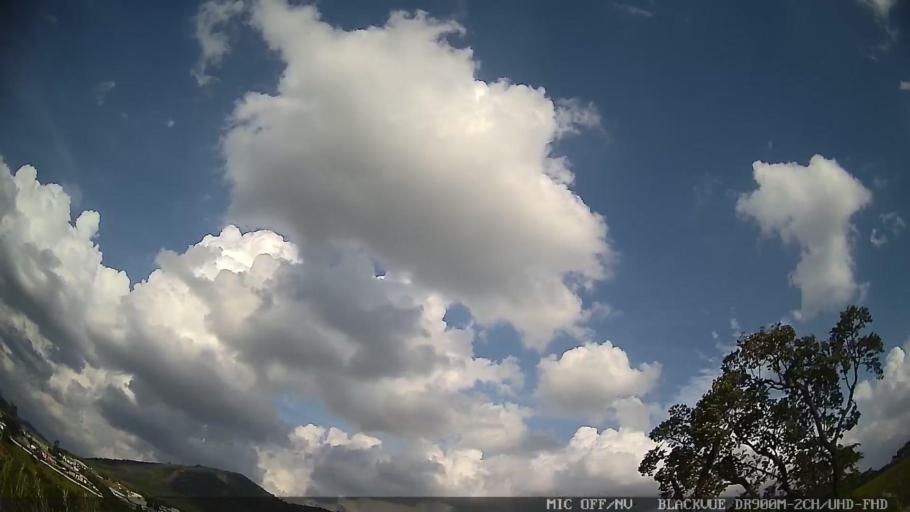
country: BR
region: Sao Paulo
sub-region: Braganca Paulista
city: Braganca Paulista
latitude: -22.9294
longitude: -46.5041
